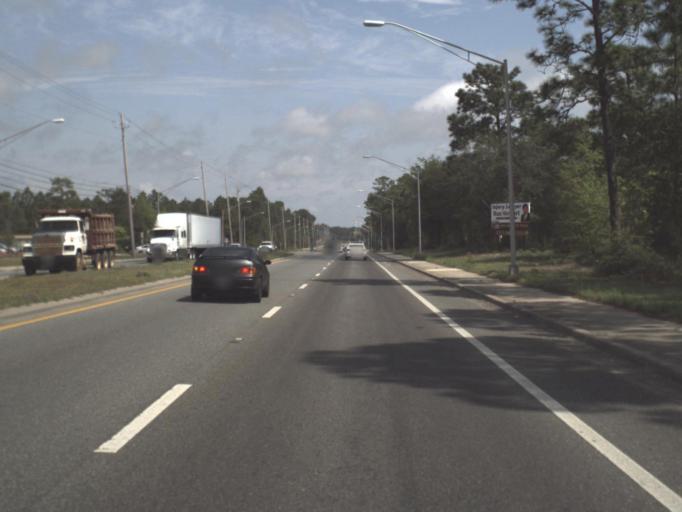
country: US
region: Florida
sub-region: Santa Rosa County
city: Navarre
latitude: 30.4238
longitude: -86.8675
